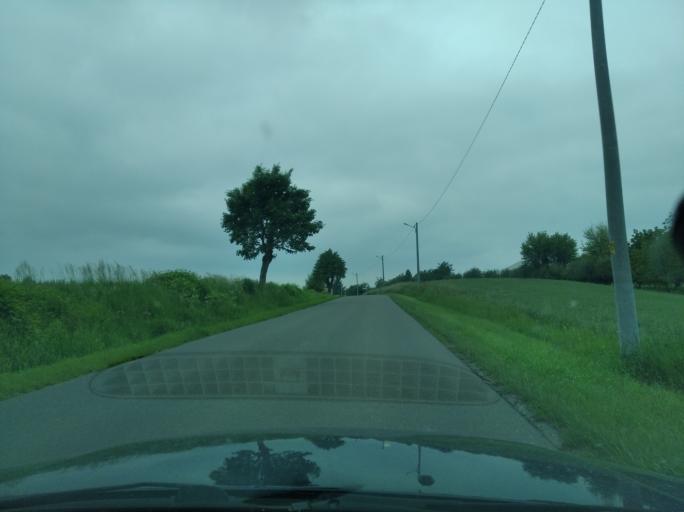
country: PL
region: Subcarpathian Voivodeship
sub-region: Powiat ropczycko-sedziszowski
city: Sedziszow Malopolski
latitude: 50.0496
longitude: 21.6908
